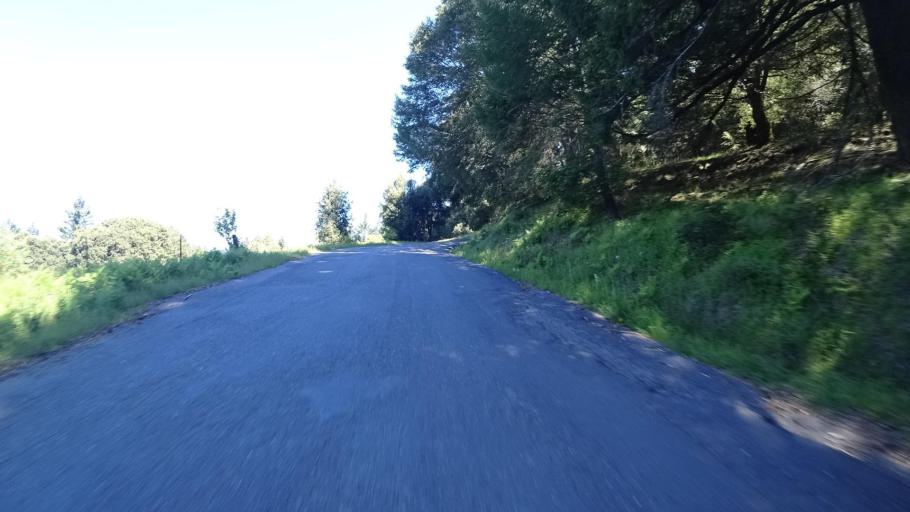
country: US
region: California
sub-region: Humboldt County
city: Redway
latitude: 40.1350
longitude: -123.9835
